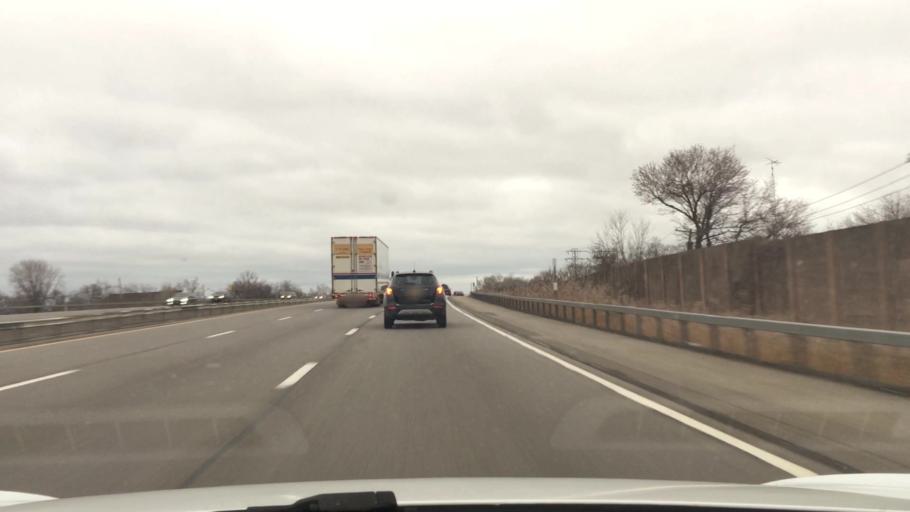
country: US
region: New York
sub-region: Erie County
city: Amherst
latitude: 43.0020
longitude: -78.8333
